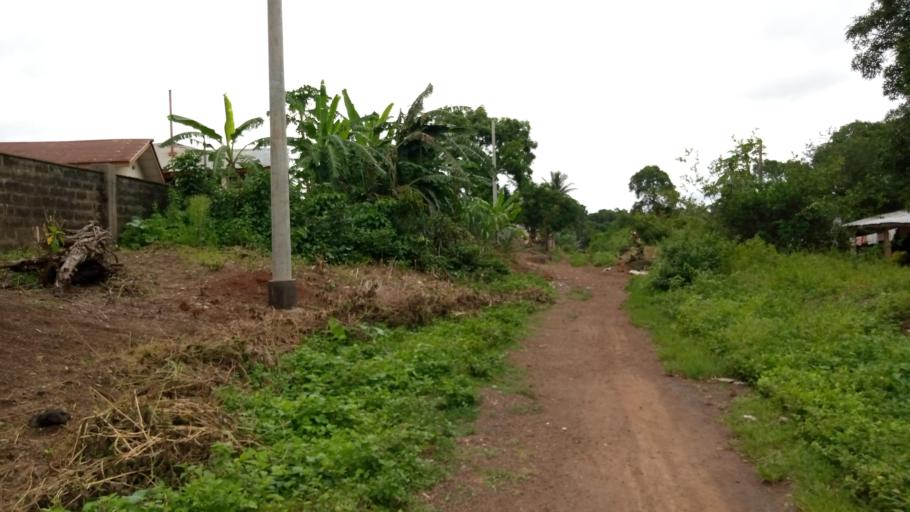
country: SL
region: Southern Province
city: Moyamba
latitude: 8.1593
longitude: -12.4348
